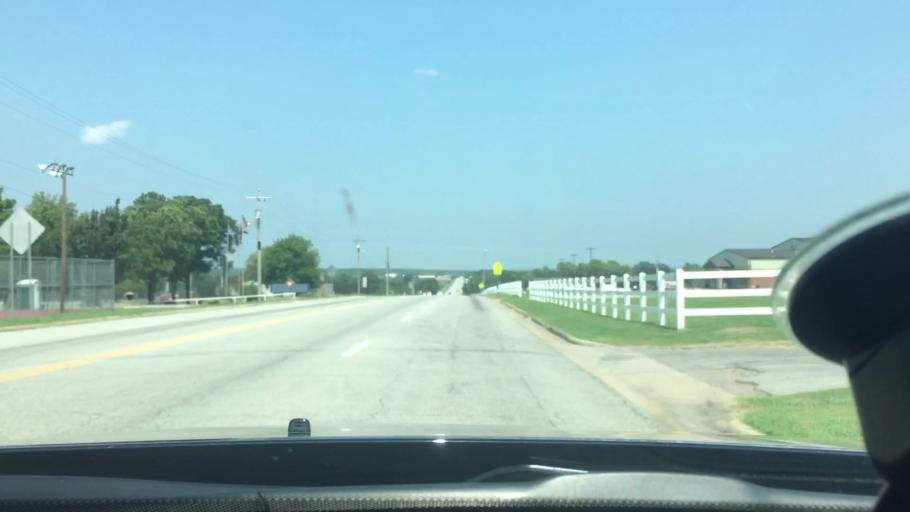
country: US
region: Oklahoma
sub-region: Atoka County
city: Atoka
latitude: 34.3765
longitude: -96.1453
